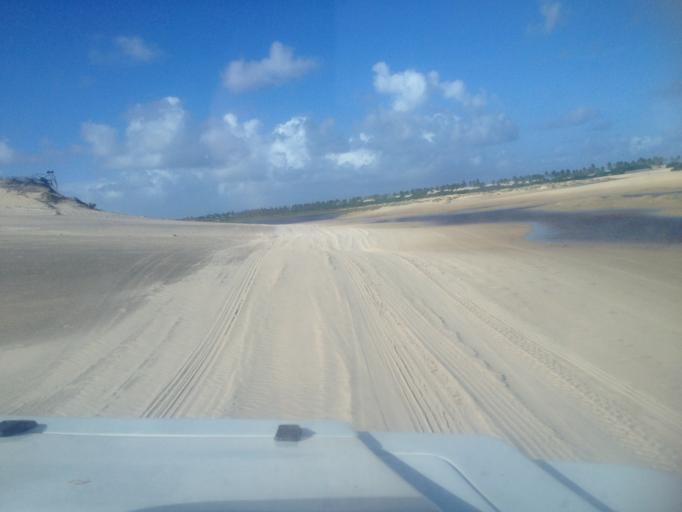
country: BR
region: Sergipe
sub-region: Indiaroba
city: Indiaroba
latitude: -11.4753
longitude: -37.3735
